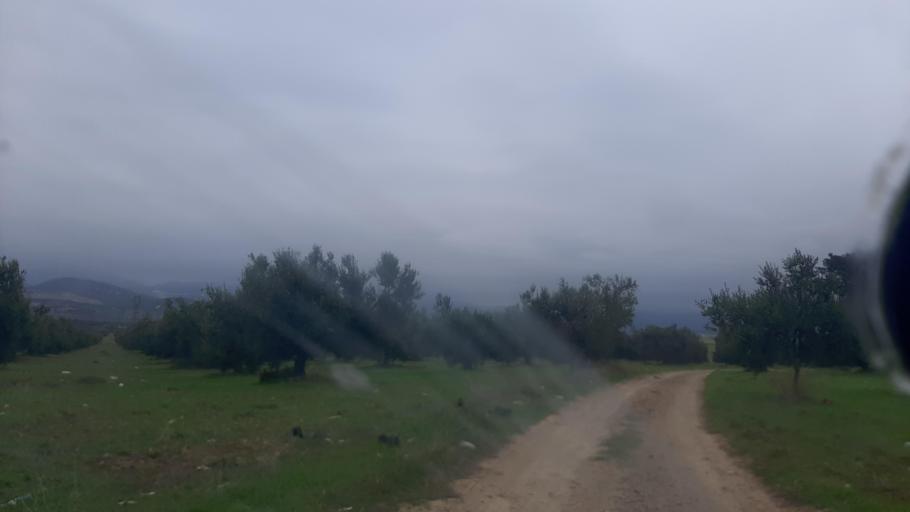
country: TN
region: Tunis
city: La Sebala du Mornag
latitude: 36.5826
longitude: 10.2897
